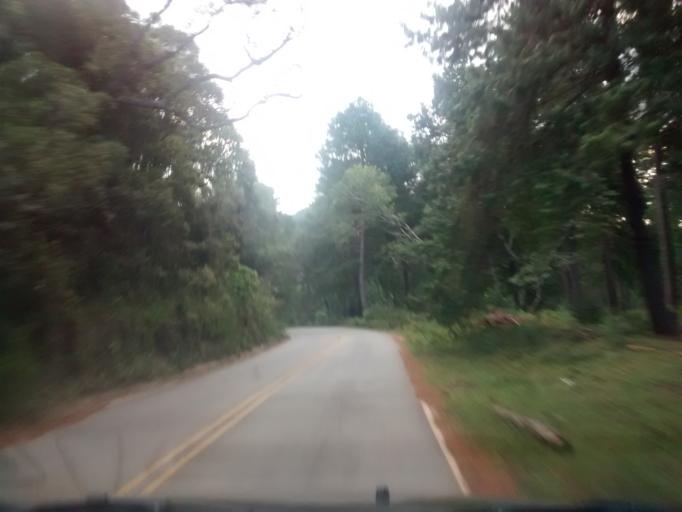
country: BR
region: Sao Paulo
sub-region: Campos Do Jordao
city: Campos do Jordao
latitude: -22.6484
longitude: -45.6267
